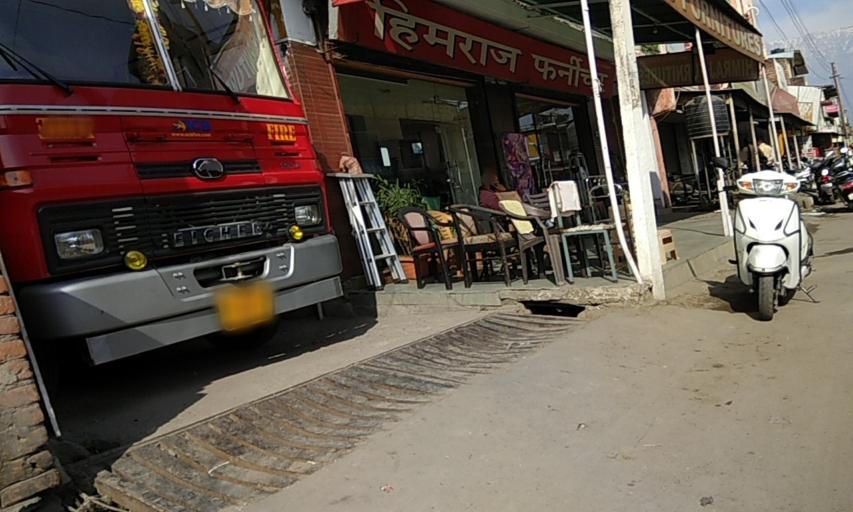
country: IN
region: Himachal Pradesh
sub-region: Kangra
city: Kangra
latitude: 32.1125
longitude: 76.2799
